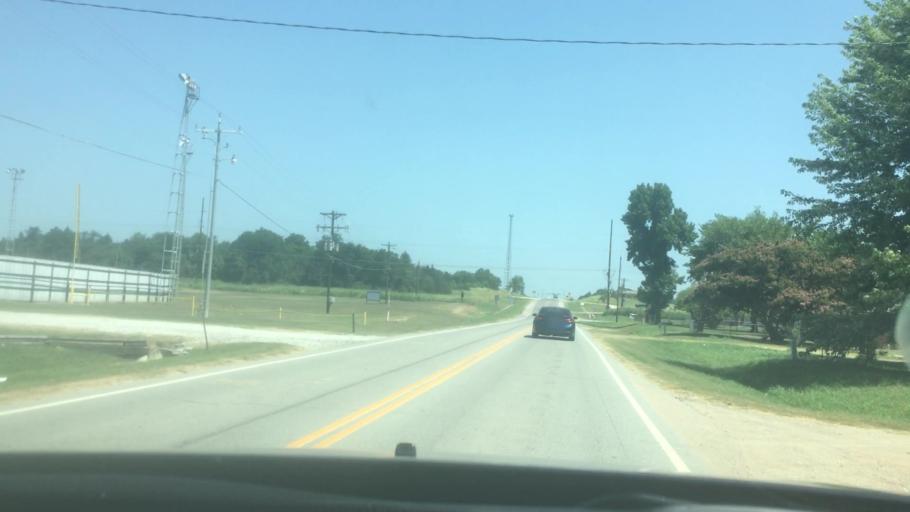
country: US
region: Oklahoma
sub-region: Coal County
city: Coalgate
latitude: 34.6053
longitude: -96.4244
